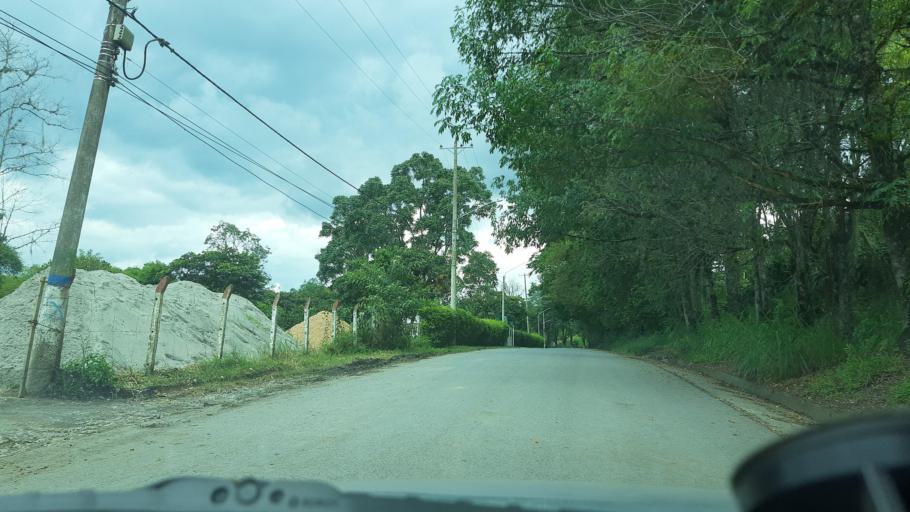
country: CO
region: Boyaca
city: Moniquira
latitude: 5.8875
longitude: -73.5771
